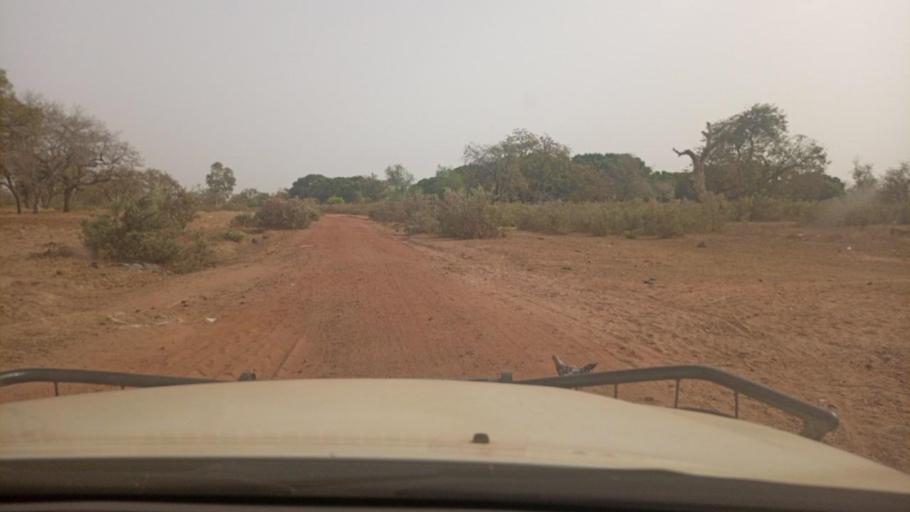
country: BF
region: Boucle du Mouhoun
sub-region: Province des Banwa
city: Salanso
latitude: 12.1109
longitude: -4.3365
